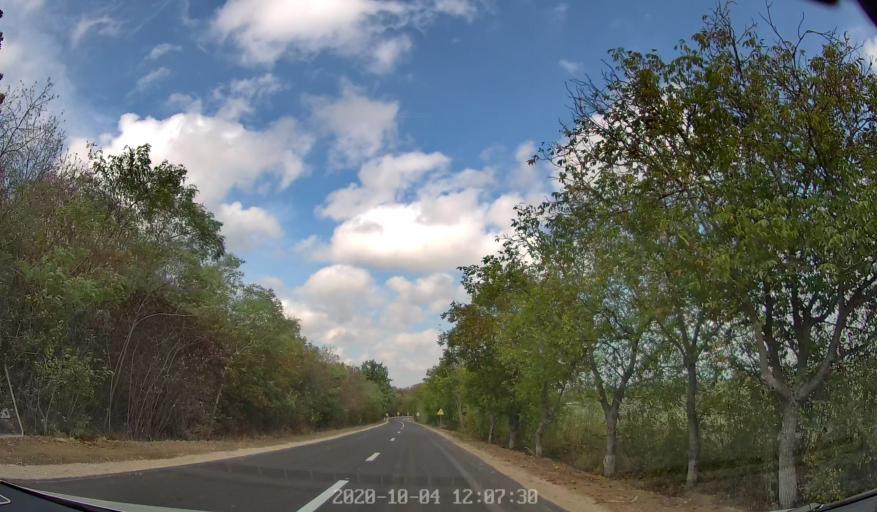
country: MD
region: Rezina
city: Saharna
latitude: 47.5865
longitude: 28.9714
